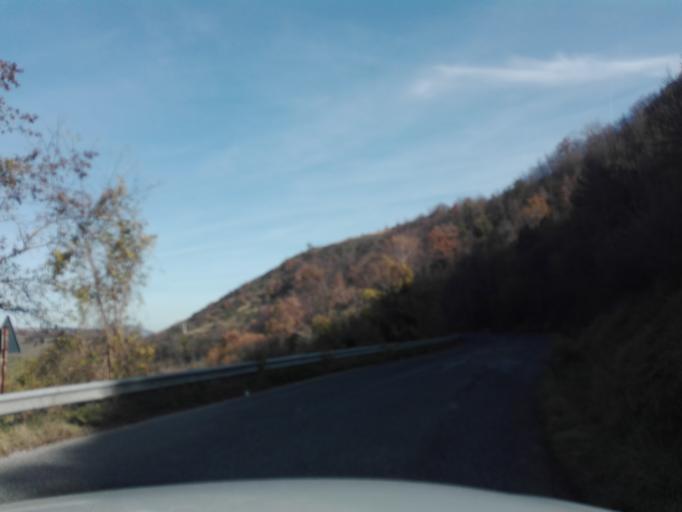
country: IT
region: Molise
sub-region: Provincia di Isernia
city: Agnone
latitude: 41.8213
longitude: 14.3743
